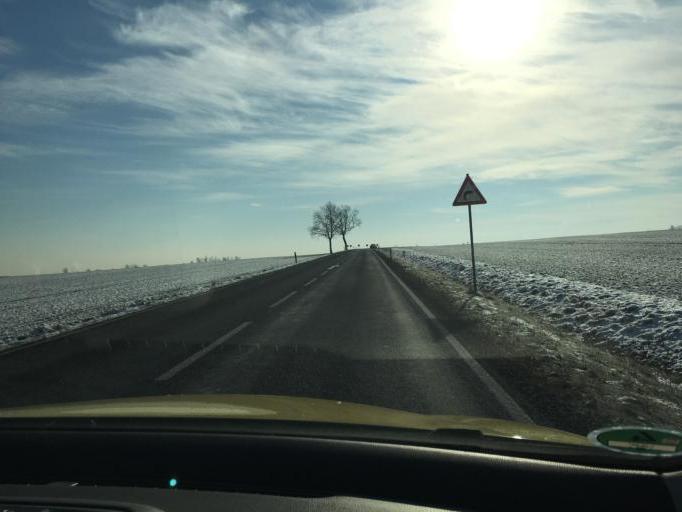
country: DE
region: Saxony
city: Otterwisch
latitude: 51.1875
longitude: 12.6136
